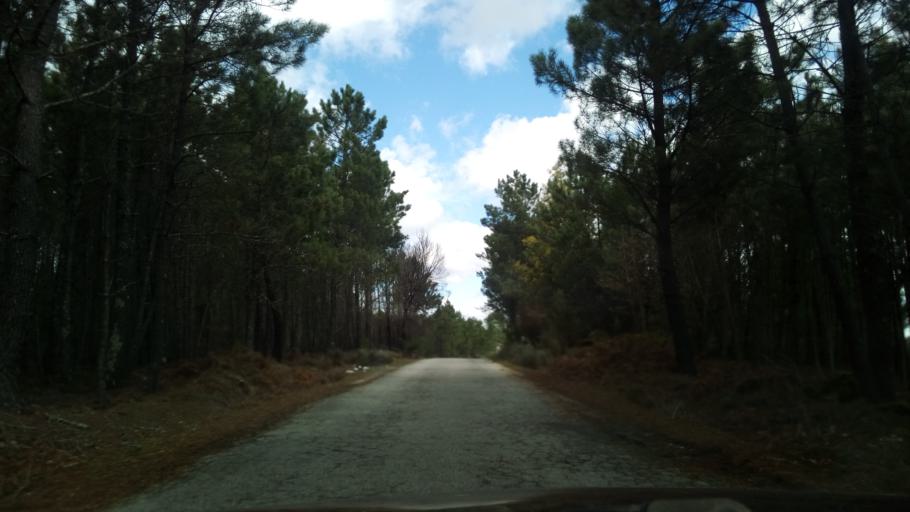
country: PT
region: Guarda
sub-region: Fornos de Algodres
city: Fornos de Algodres
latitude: 40.6587
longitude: -7.5076
